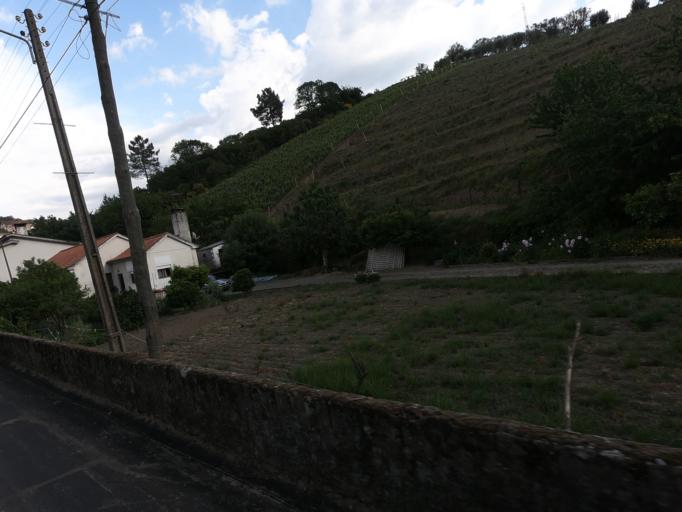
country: PT
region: Vila Real
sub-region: Santa Marta de Penaguiao
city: Santa Marta de Penaguiao
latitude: 41.2208
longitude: -7.7212
